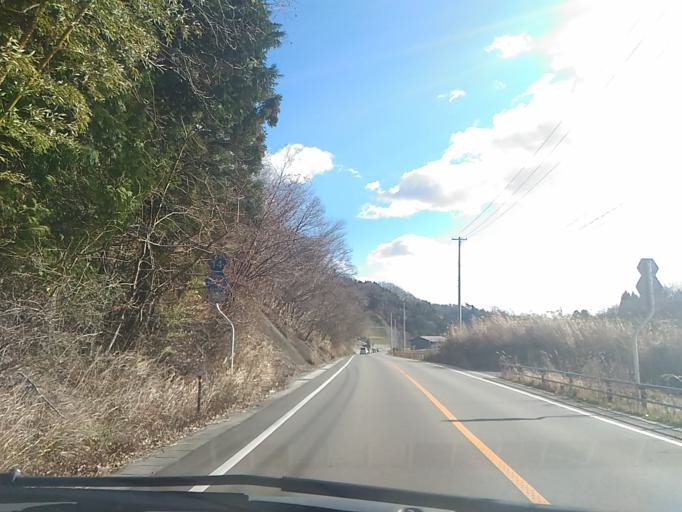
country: JP
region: Fukushima
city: Iwaki
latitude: 37.0147
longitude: 140.7692
